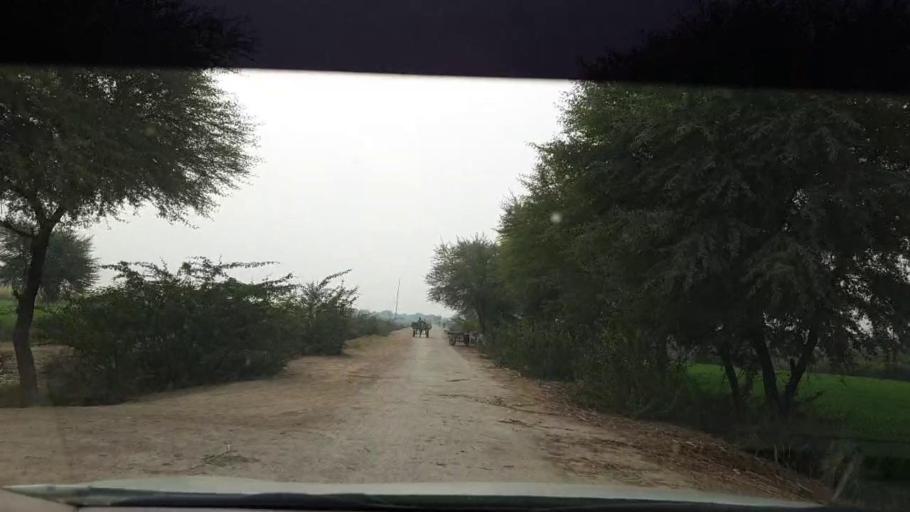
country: PK
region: Sindh
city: Berani
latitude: 25.8616
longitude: 68.8365
